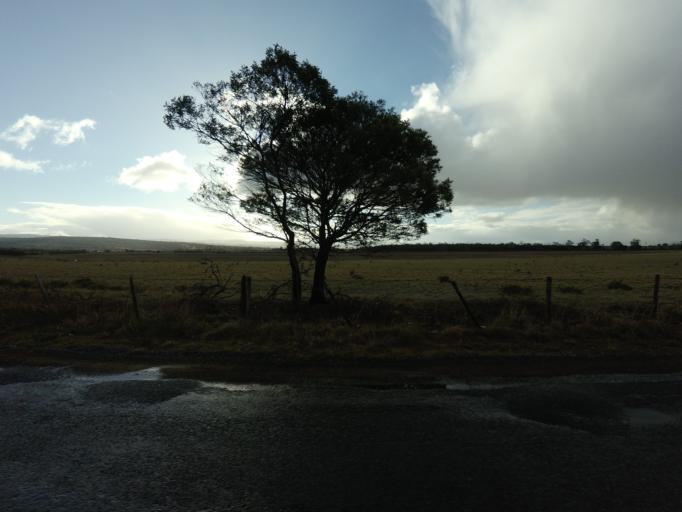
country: AU
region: Tasmania
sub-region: Break O'Day
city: St Helens
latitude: -42.0934
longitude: 148.0739
